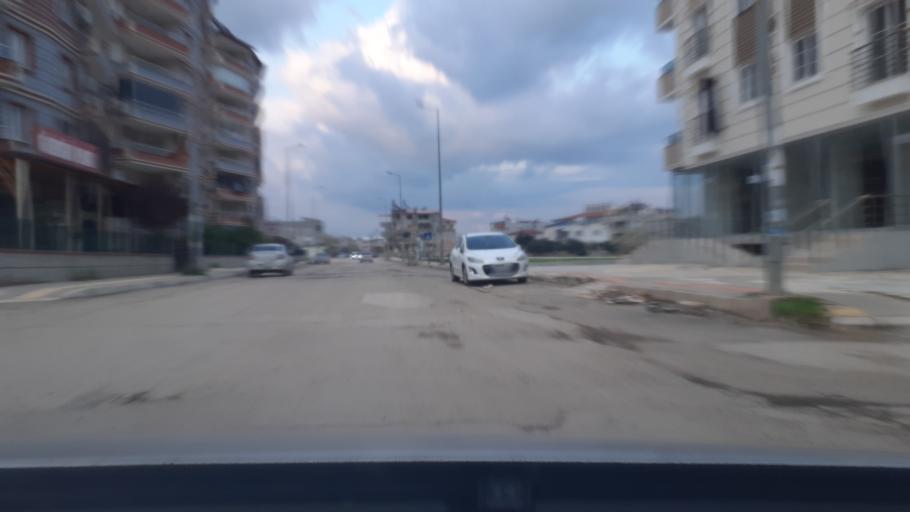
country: TR
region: Hatay
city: Kirikhan
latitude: 36.4833
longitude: 36.3538
